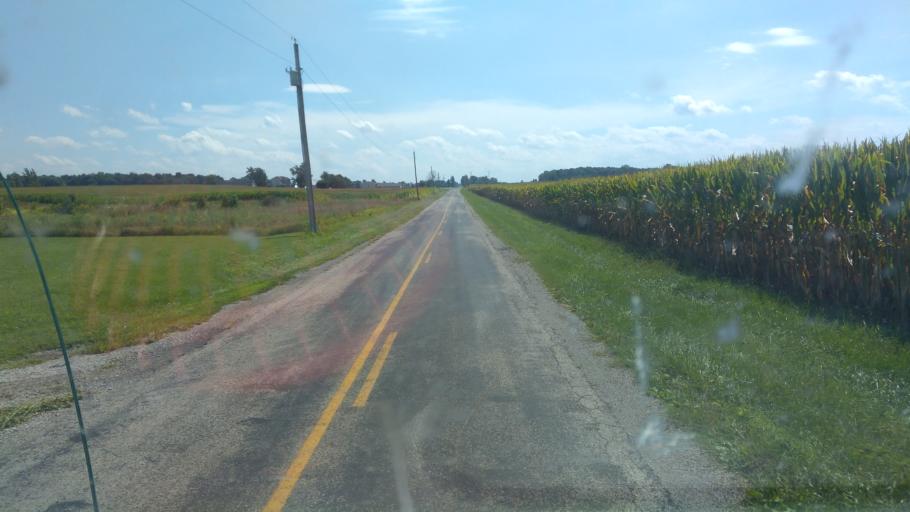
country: US
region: Ohio
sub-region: Wyandot County
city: Upper Sandusky
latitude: 40.6475
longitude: -83.3430
